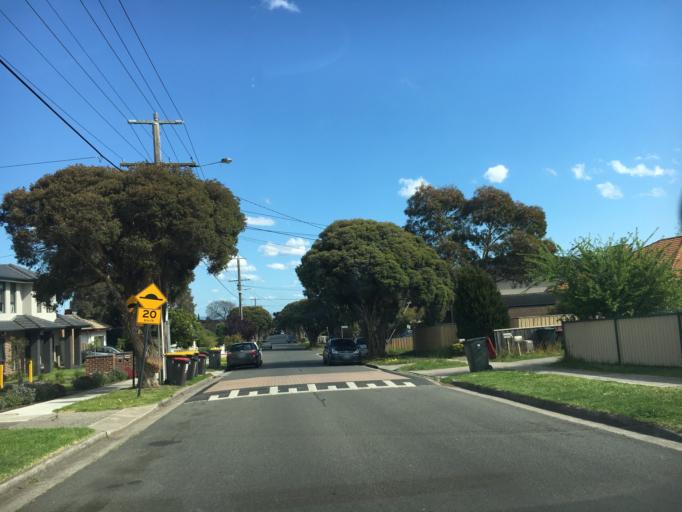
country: AU
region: Victoria
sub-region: Monash
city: Clayton
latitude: -37.9191
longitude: 145.1298
